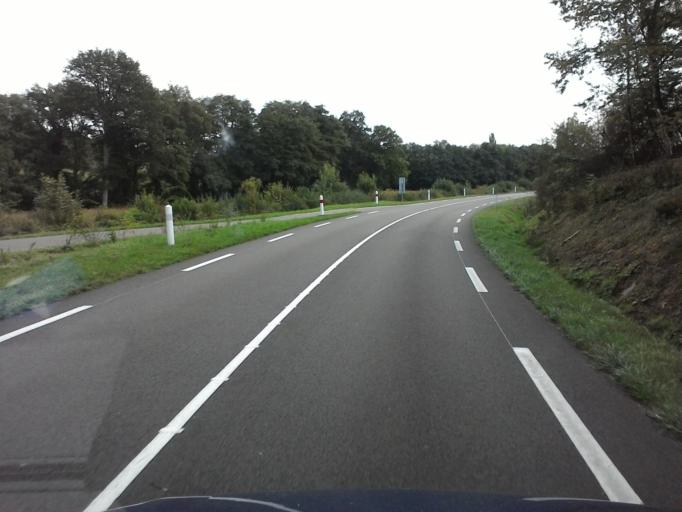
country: FR
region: Bourgogne
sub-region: Departement de Saone-et-Loire
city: Saint-Eusebe
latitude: 46.5820
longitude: 4.5201
